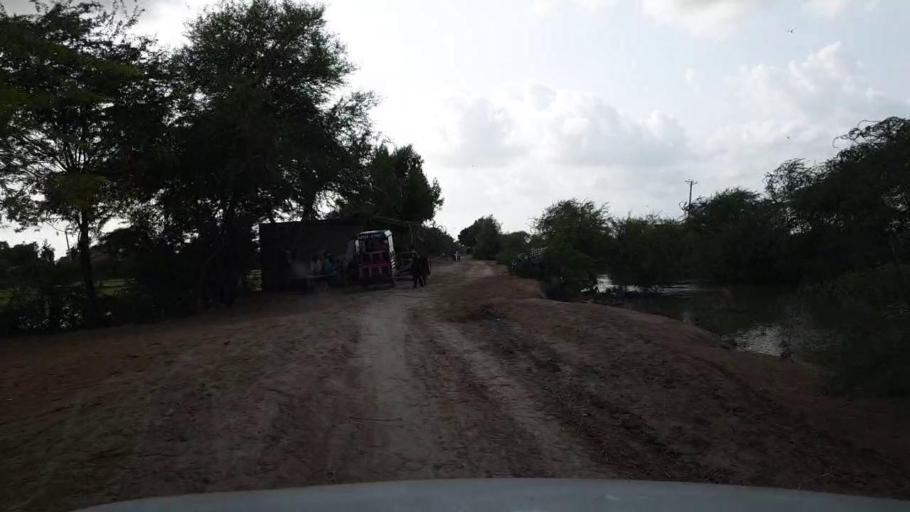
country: PK
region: Sindh
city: Kario
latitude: 24.7582
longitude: 68.6074
